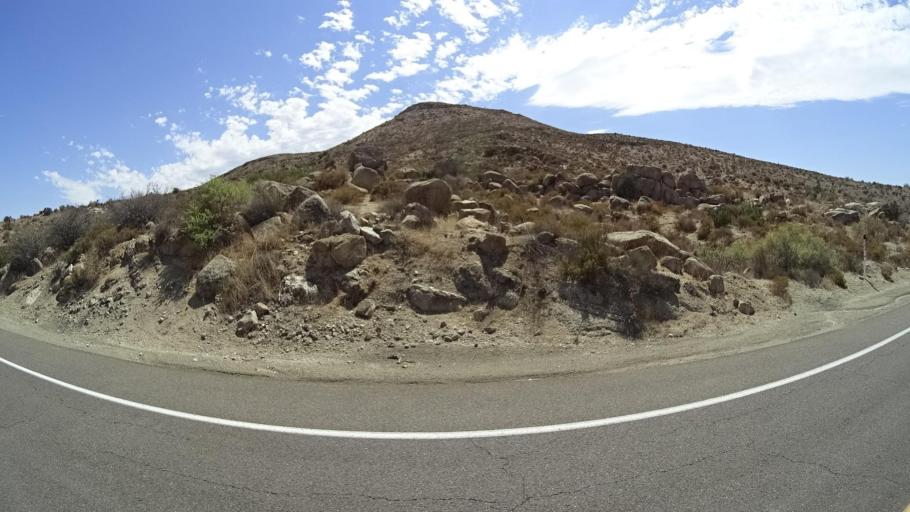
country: MX
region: Baja California
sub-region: Tecate
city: Cereso del Hongo
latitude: 32.6255
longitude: -116.1446
